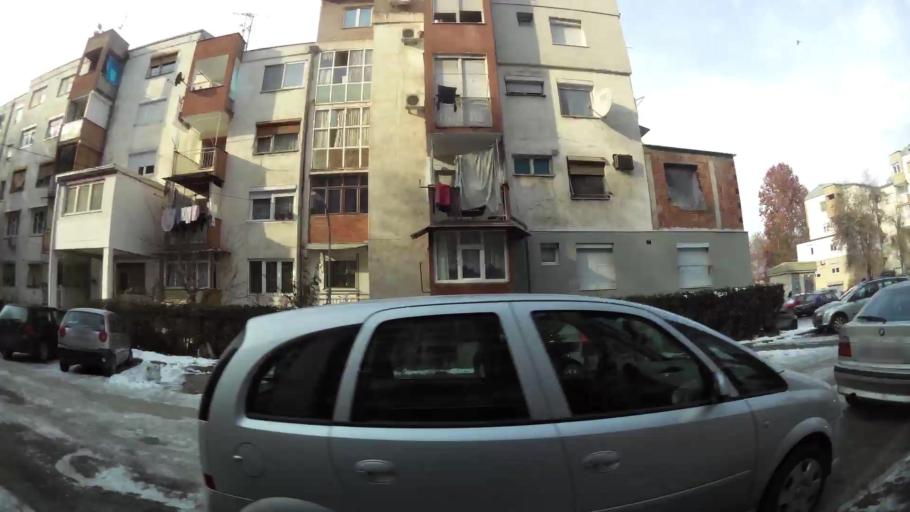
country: MK
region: Cair
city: Cair
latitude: 42.0210
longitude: 21.4320
